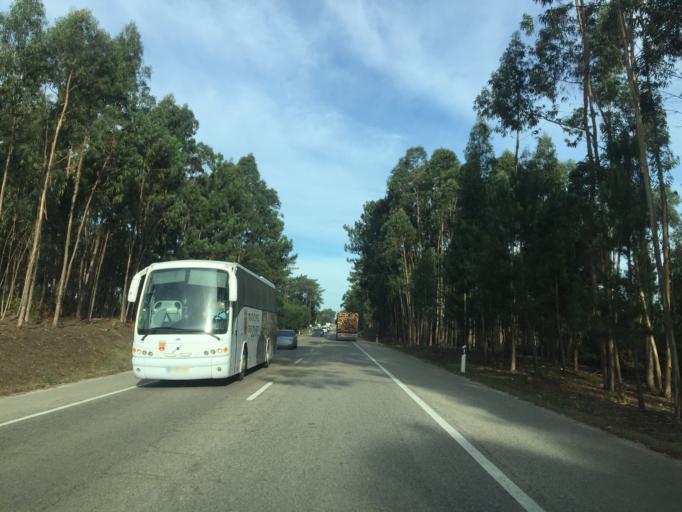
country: PT
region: Leiria
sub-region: Pombal
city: Lourical
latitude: 40.0144
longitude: -8.8085
